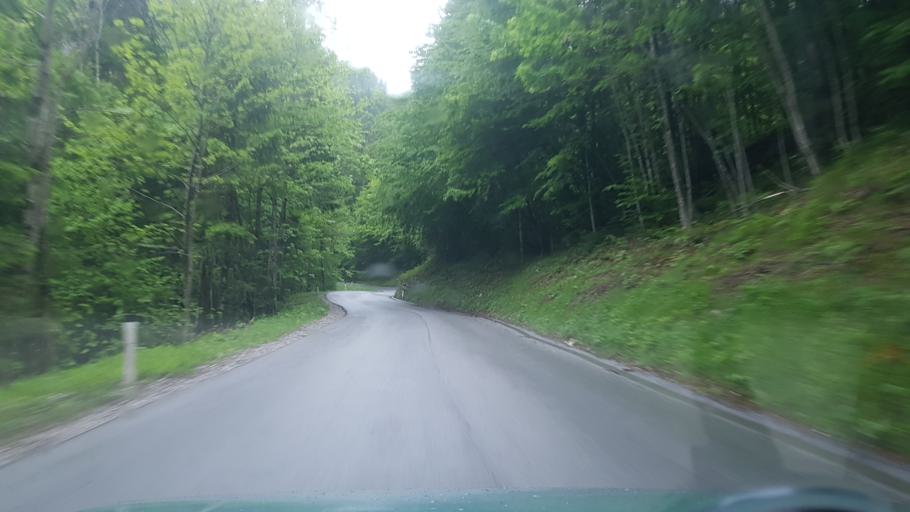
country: SI
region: Bohinj
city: Bohinjska Bistrica
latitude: 46.2713
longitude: 13.9953
